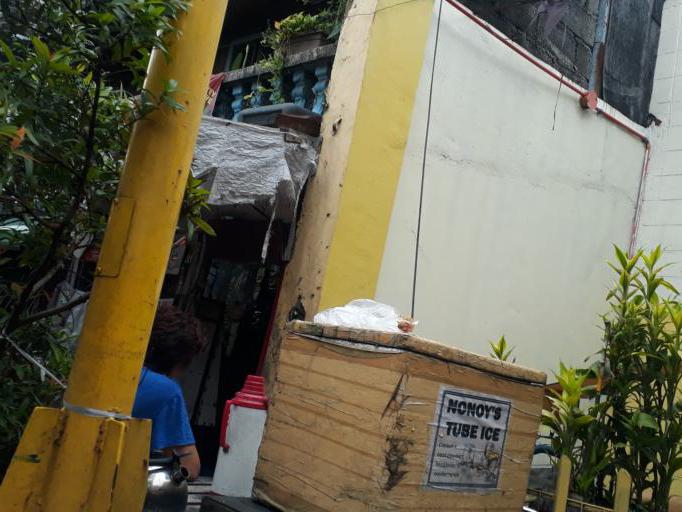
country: PH
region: Calabarzon
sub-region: Province of Rizal
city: Navotas
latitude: 14.6556
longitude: 120.9477
